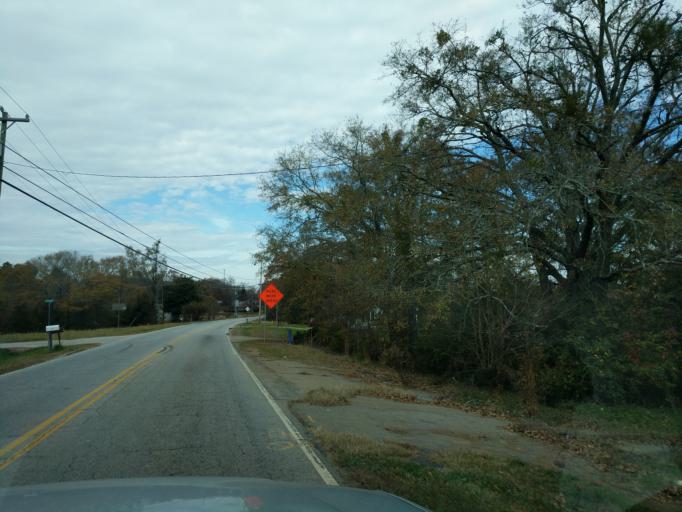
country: US
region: South Carolina
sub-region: Pickens County
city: Easley
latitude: 34.7763
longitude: -82.5767
